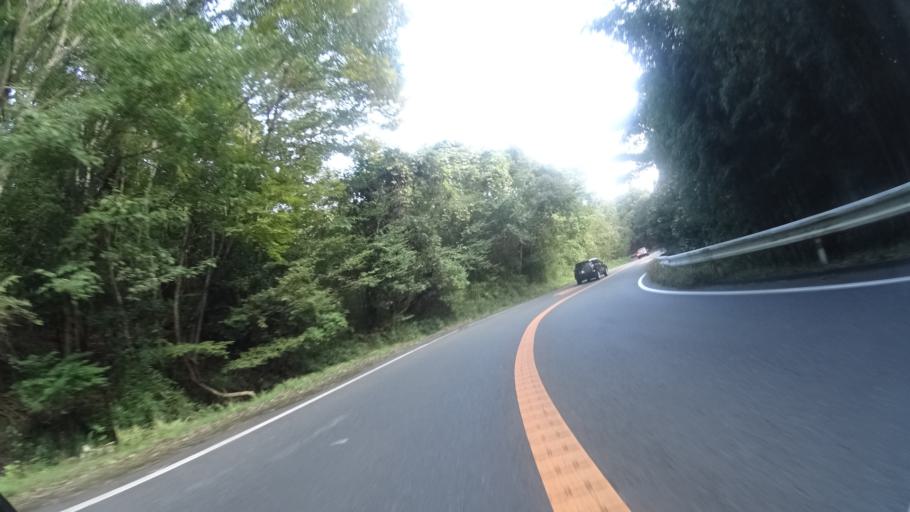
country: JP
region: Oita
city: Beppu
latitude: 33.2710
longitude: 131.4285
